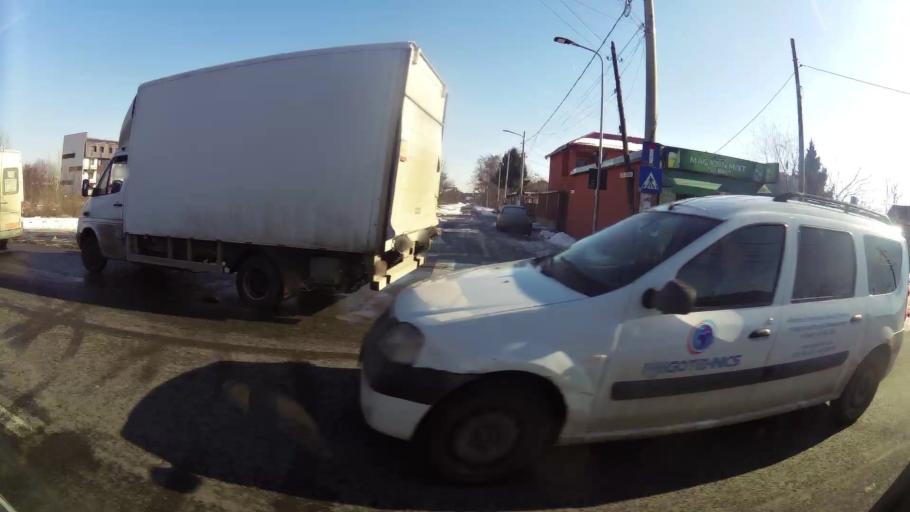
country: RO
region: Ilfov
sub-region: Comuna Magurele
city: Magurele
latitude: 44.3847
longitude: 26.0469
